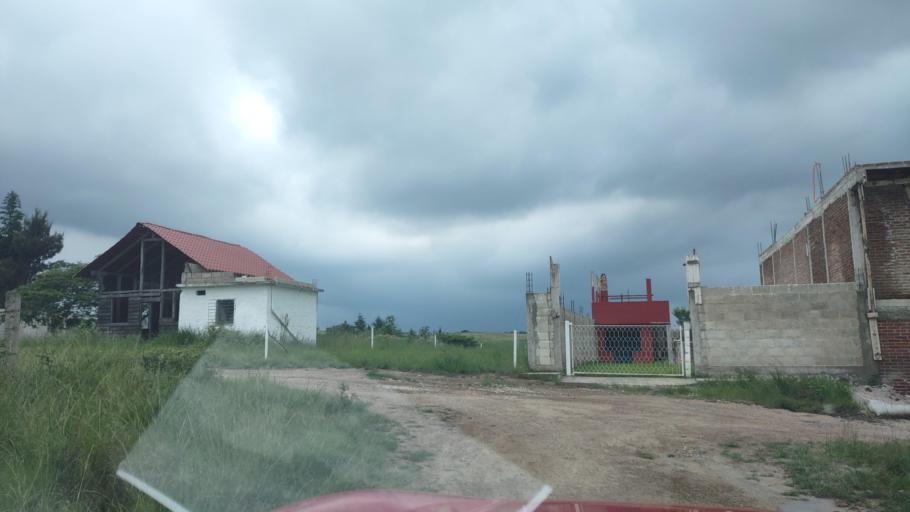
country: MX
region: Veracruz
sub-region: Emiliano Zapata
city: Dos Rios
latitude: 19.4840
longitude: -96.8262
